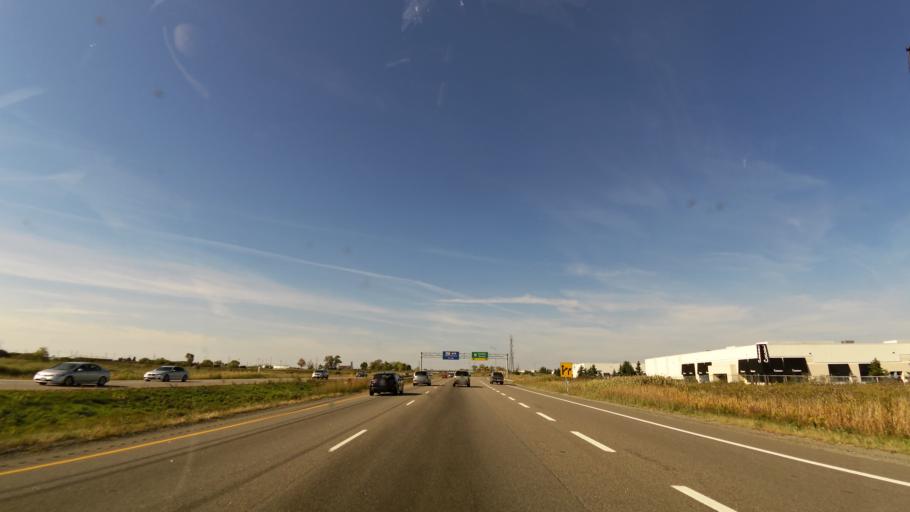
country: CA
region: Ontario
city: Oakville
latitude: 43.5082
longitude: -79.6866
